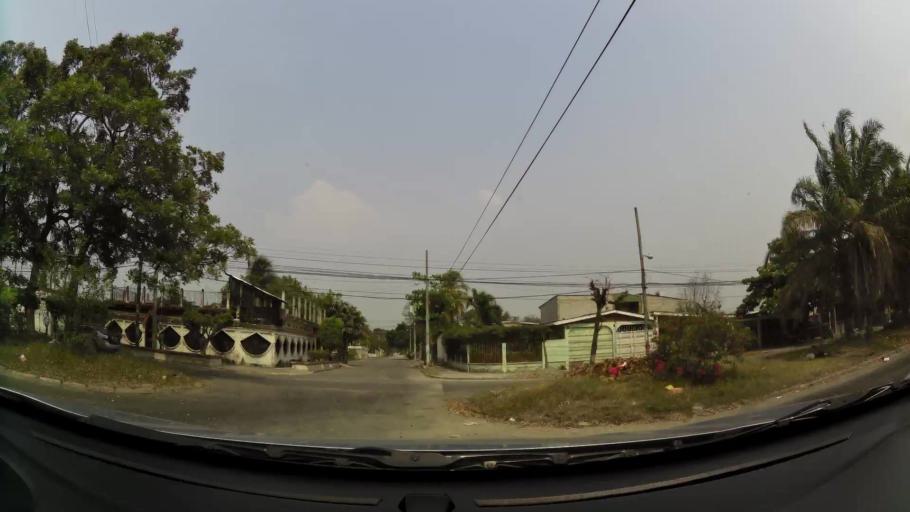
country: HN
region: Cortes
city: San Pedro Sula
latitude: 15.4829
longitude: -88.0174
